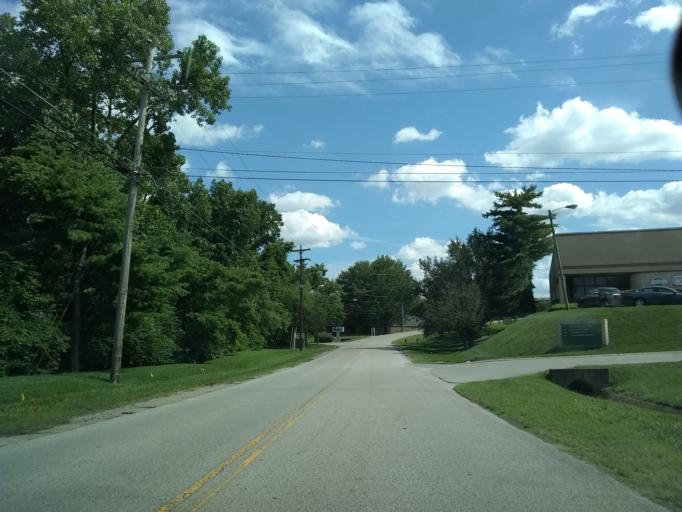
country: US
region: Tennessee
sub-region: Davidson County
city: Nashville
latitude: 36.1480
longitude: -86.6973
